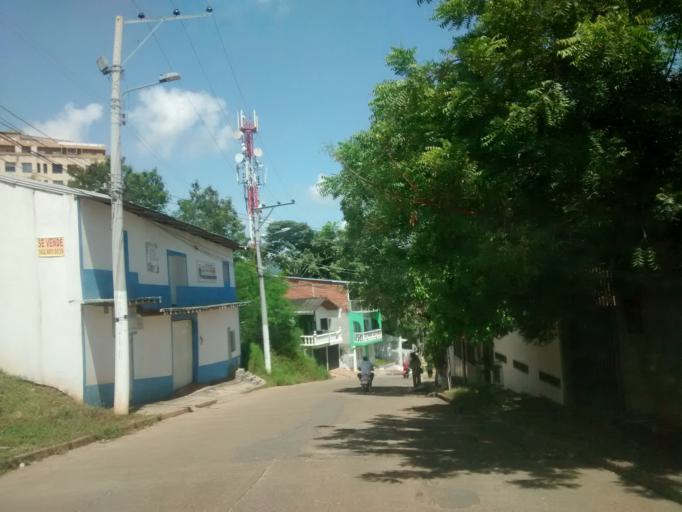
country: CO
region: Cundinamarca
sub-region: Girardot
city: Girardot City
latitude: 4.2969
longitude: -74.7993
